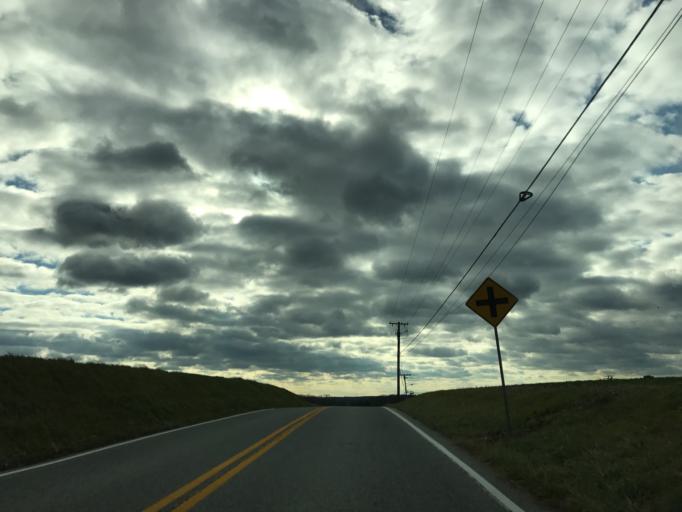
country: US
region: Pennsylvania
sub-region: York County
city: Stewartstown
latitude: 39.6520
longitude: -76.6117
